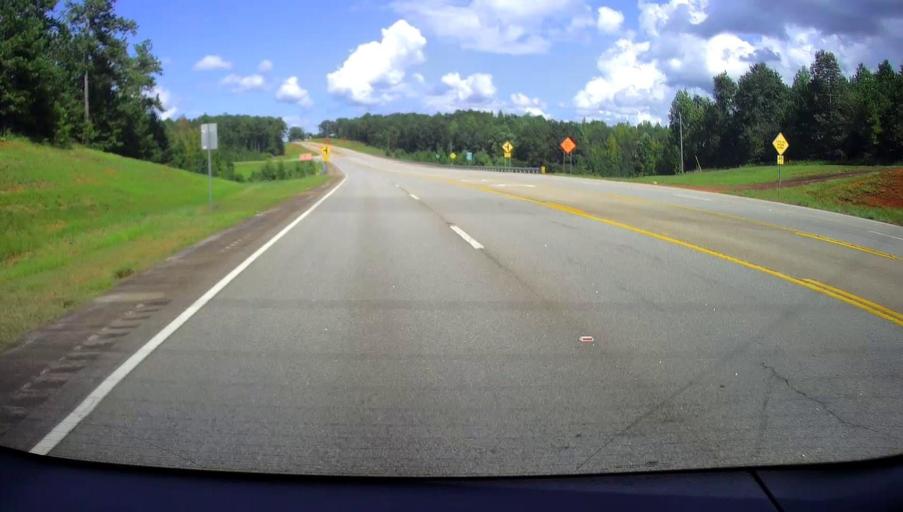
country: US
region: Georgia
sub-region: Upson County
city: Thomaston
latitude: 32.8887
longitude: -84.3012
